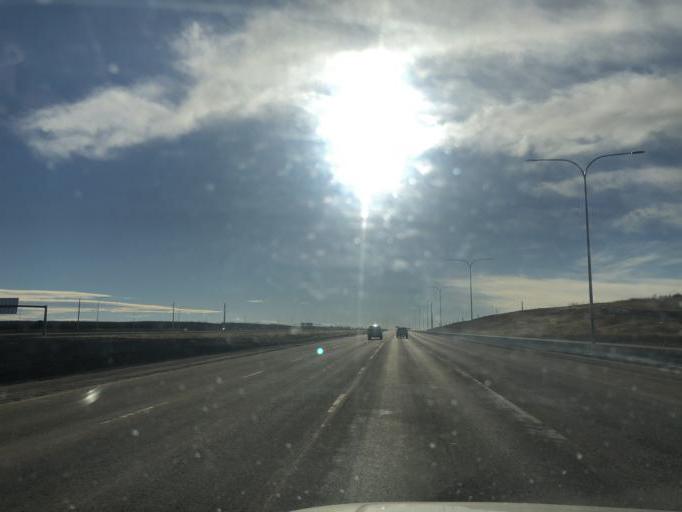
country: CA
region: Alberta
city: Calgary
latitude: 50.9758
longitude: -114.1577
